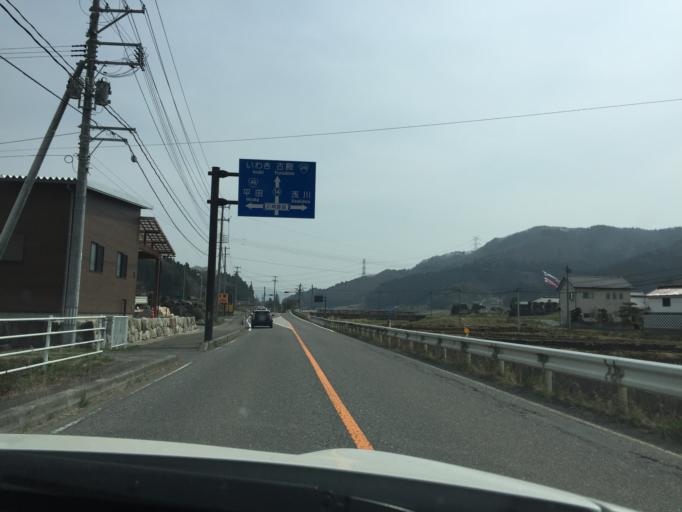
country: JP
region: Fukushima
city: Ishikawa
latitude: 37.1346
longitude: 140.4938
